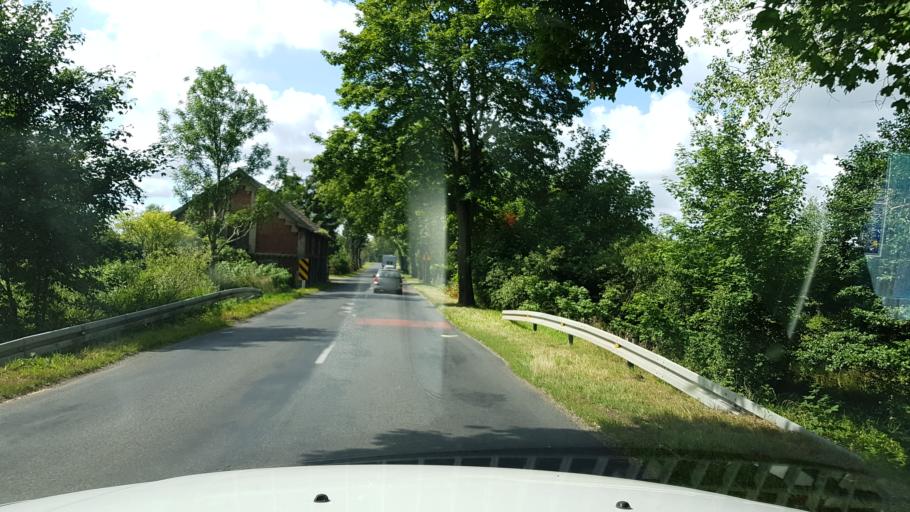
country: PL
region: West Pomeranian Voivodeship
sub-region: Powiat gryficki
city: Brojce
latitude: 54.0621
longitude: 15.3915
